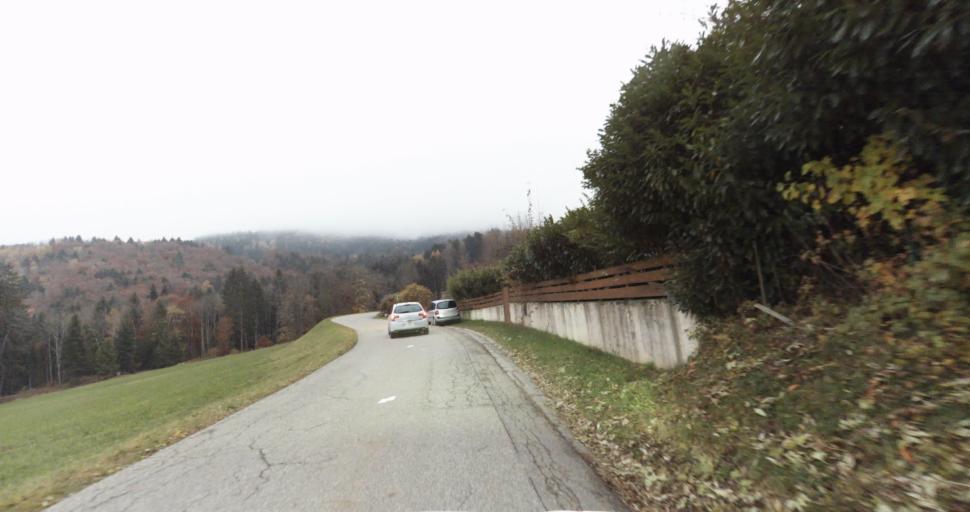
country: FR
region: Rhone-Alpes
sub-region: Departement de la Haute-Savoie
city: Saint-Jorioz
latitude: 45.7903
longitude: 6.1492
